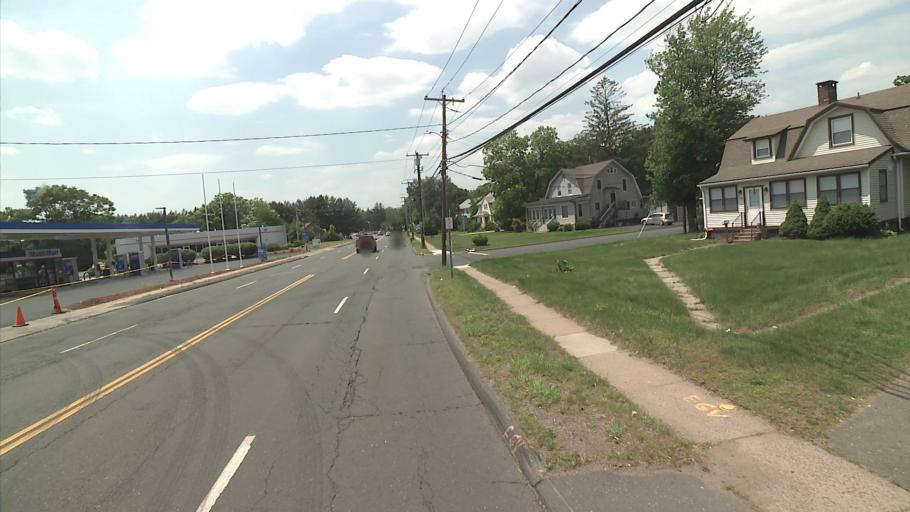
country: US
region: Connecticut
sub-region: Hartford County
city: East Hartford
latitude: 41.7627
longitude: -72.6228
